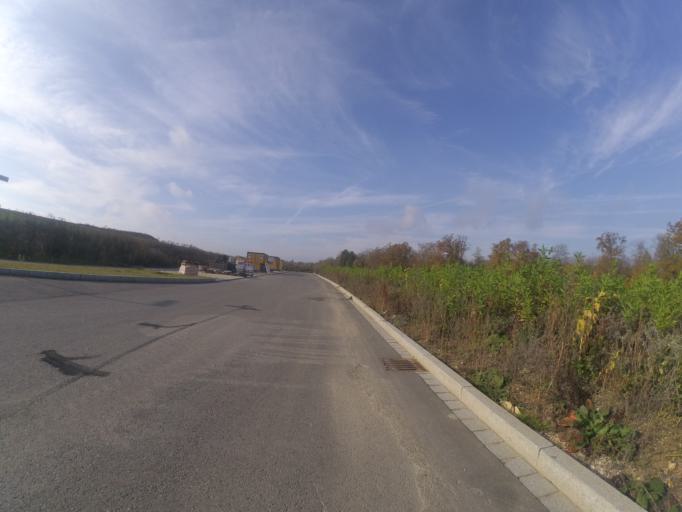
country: DE
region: Baden-Wuerttemberg
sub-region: Tuebingen Region
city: Dornstadt
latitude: 48.4262
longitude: 9.9320
